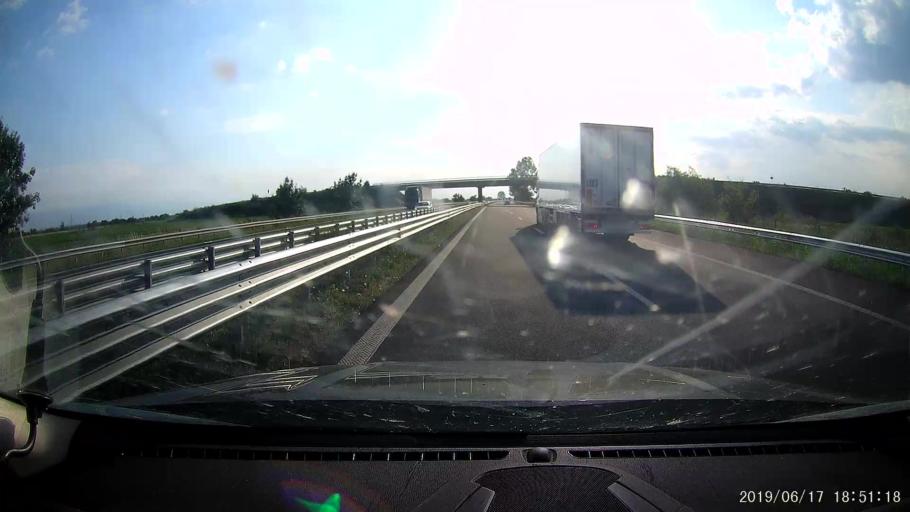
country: BG
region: Plovdiv
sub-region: Obshtina Rakovski
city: Rakovski
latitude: 42.2136
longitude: 24.9764
